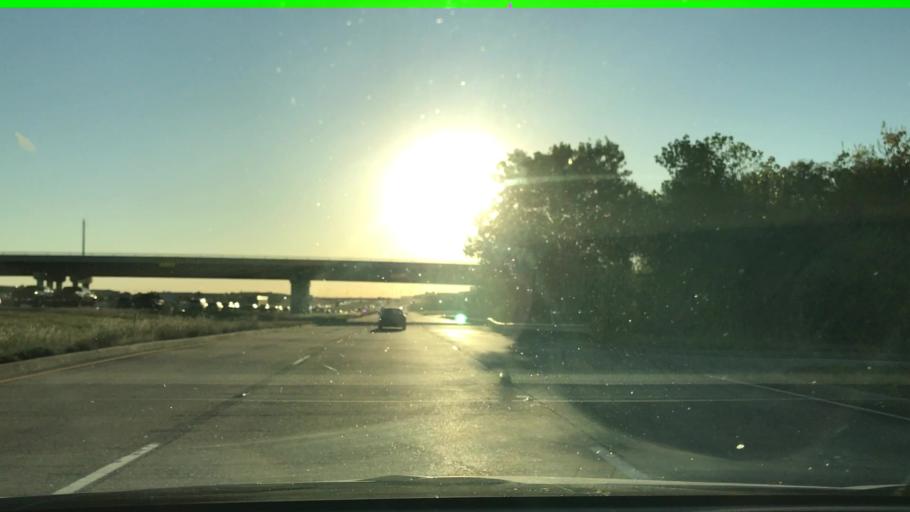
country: US
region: Texas
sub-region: Dallas County
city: Coppell
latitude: 32.9190
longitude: -96.9767
